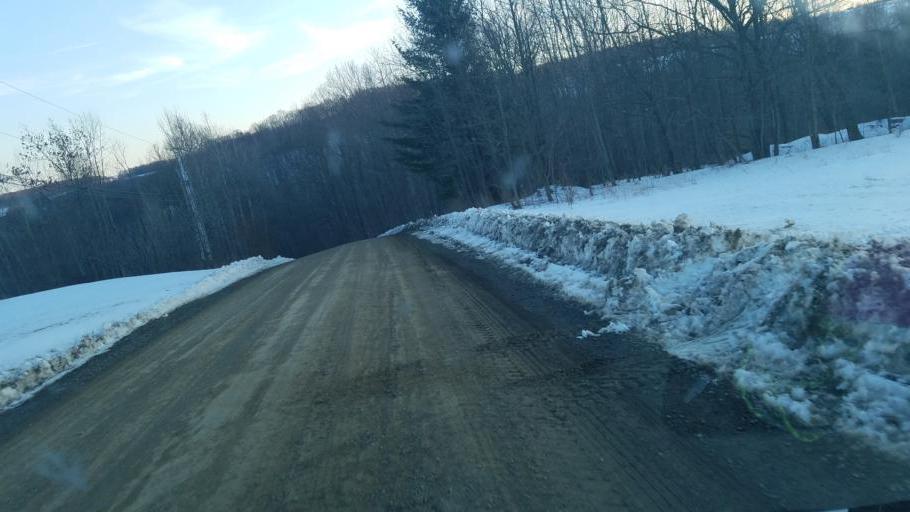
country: US
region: Pennsylvania
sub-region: Tioga County
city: Westfield
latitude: 42.0250
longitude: -77.6196
